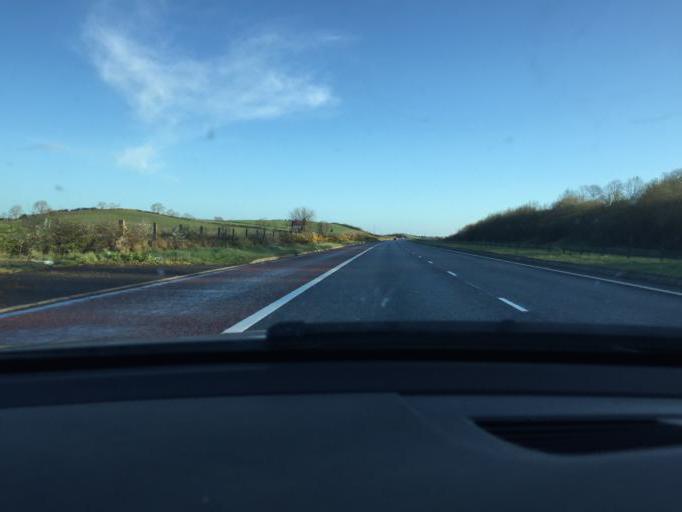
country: GB
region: Northern Ireland
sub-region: Banbridge District
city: Banbridge
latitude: 54.2945
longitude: -6.2990
